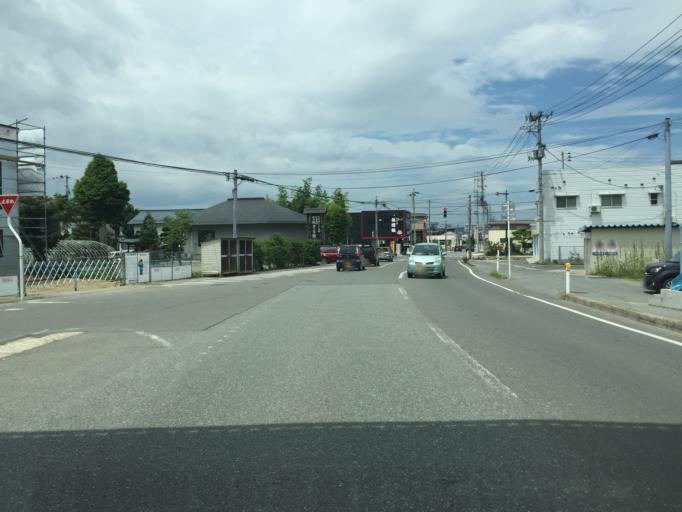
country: JP
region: Yamagata
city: Yonezawa
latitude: 37.9054
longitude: 140.1279
